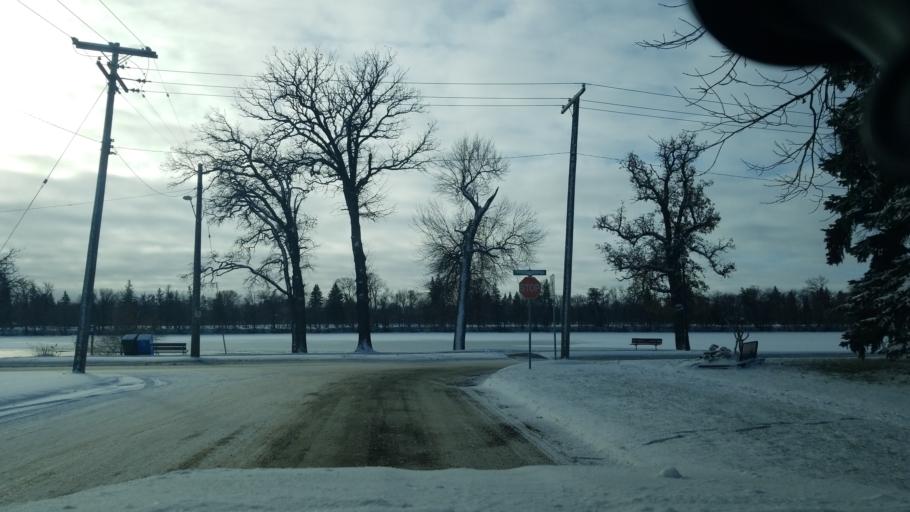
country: CA
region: Manitoba
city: Portage la Prairie
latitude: 49.9707
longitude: -98.3022
